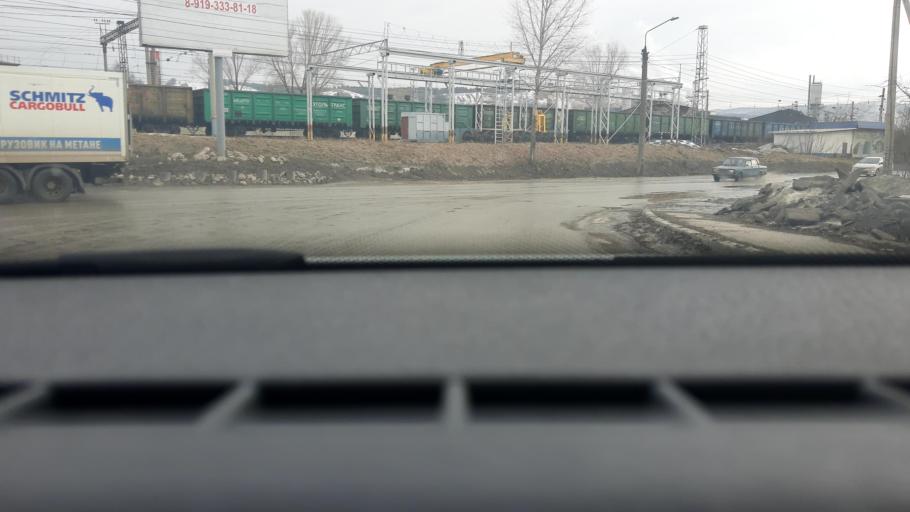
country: RU
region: Chelyabinsk
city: Asha
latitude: 54.9963
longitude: 57.2616
